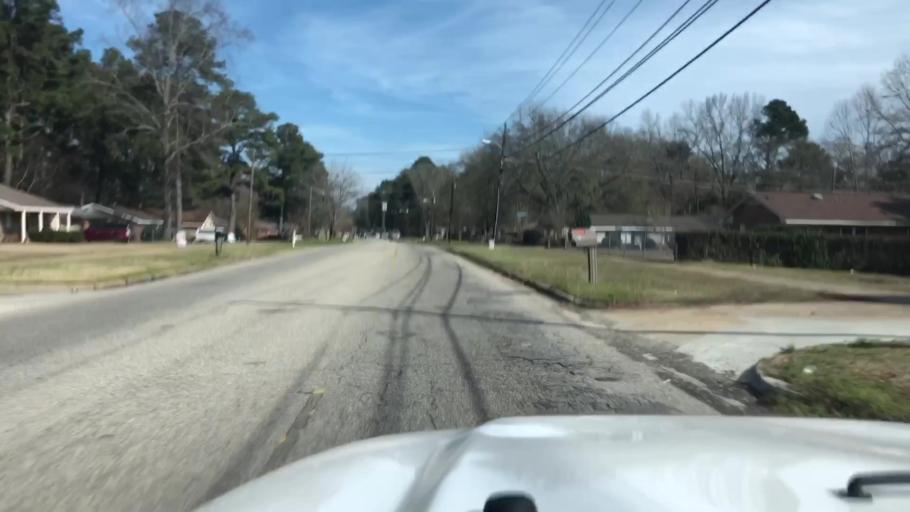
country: US
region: Alabama
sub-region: Elmore County
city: Blue Ridge
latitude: 32.3940
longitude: -86.1944
